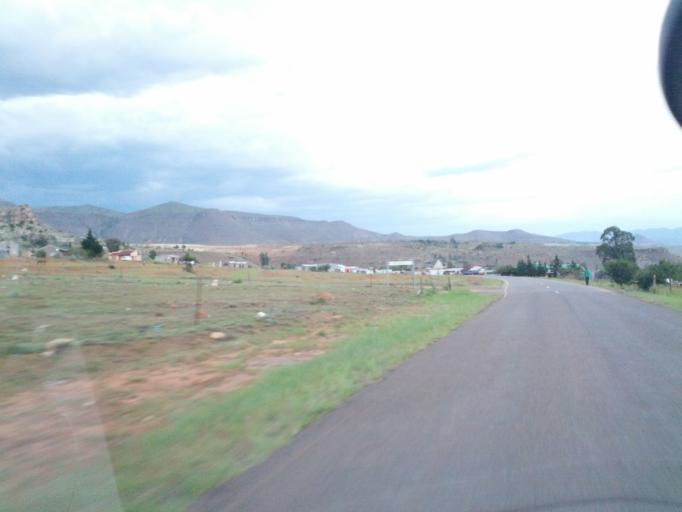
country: LS
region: Qacha's Nek
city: Qacha's Nek
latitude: -30.0476
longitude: 28.3658
